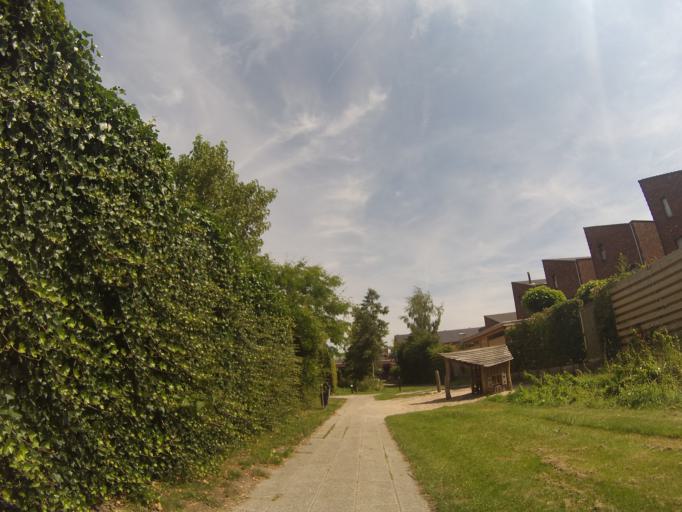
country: NL
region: Utrecht
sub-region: Gemeente Amersfoort
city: Randenbroek
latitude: 52.1938
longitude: 5.4288
